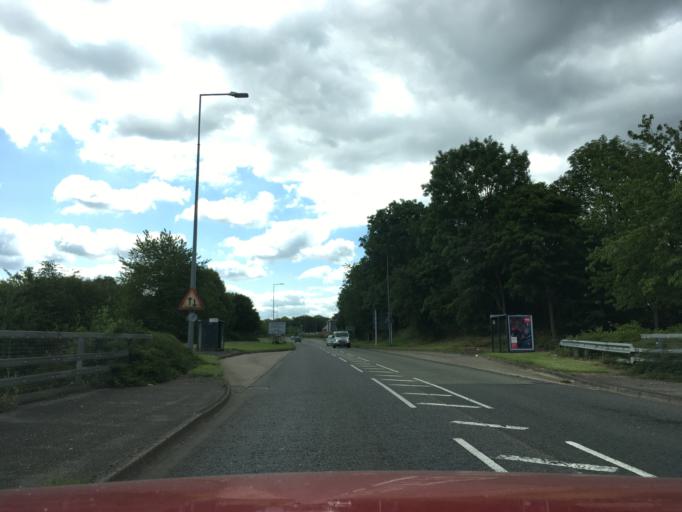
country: GB
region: England
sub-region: Milton Keynes
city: Bradwell
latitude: 52.0571
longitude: -0.7727
